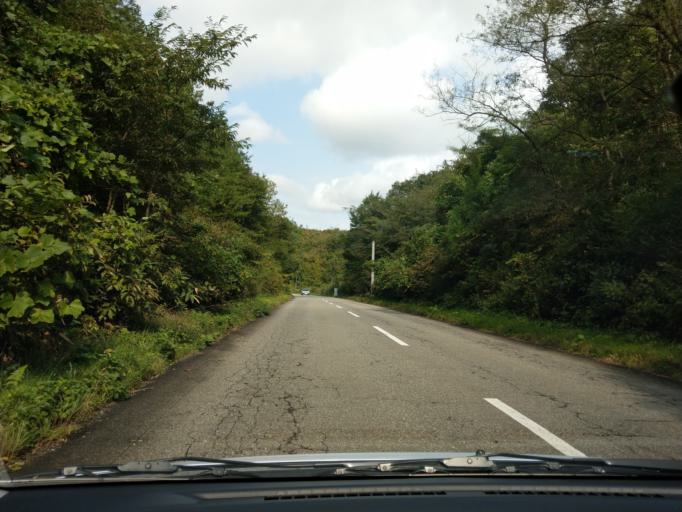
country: JP
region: Akita
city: Omagari
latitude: 39.4905
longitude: 140.3138
